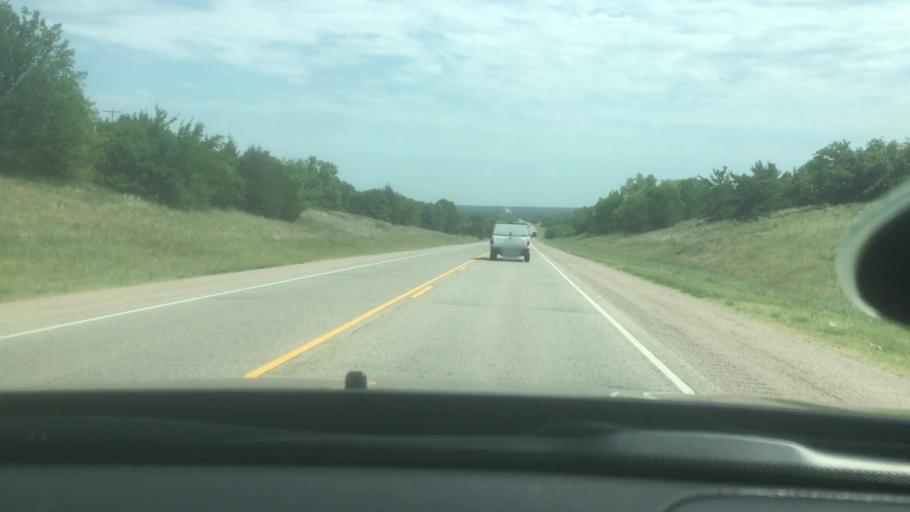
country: US
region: Oklahoma
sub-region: Seminole County
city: Maud
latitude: 35.0589
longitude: -96.9315
